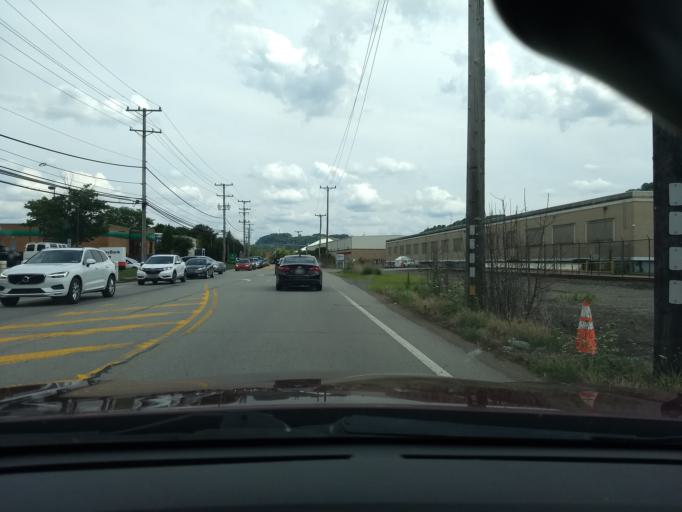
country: US
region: Pennsylvania
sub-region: Allegheny County
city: Aspinwall
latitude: 40.4871
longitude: -79.8949
